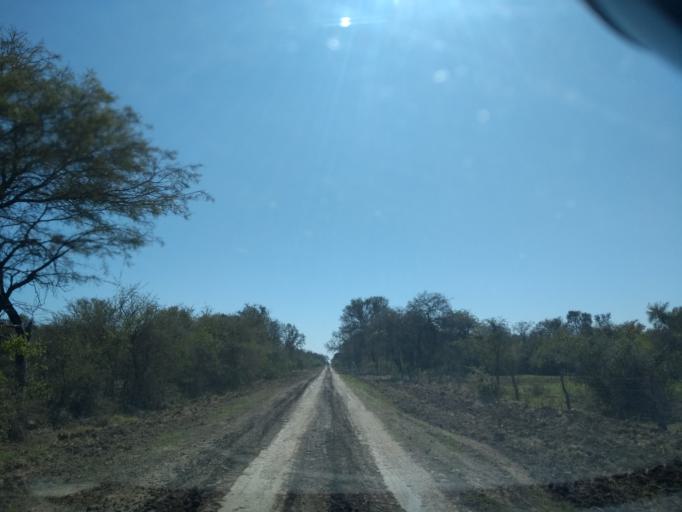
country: AR
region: Chaco
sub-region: Departamento de Quitilipi
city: Quitilipi
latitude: -26.7311
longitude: -60.2318
